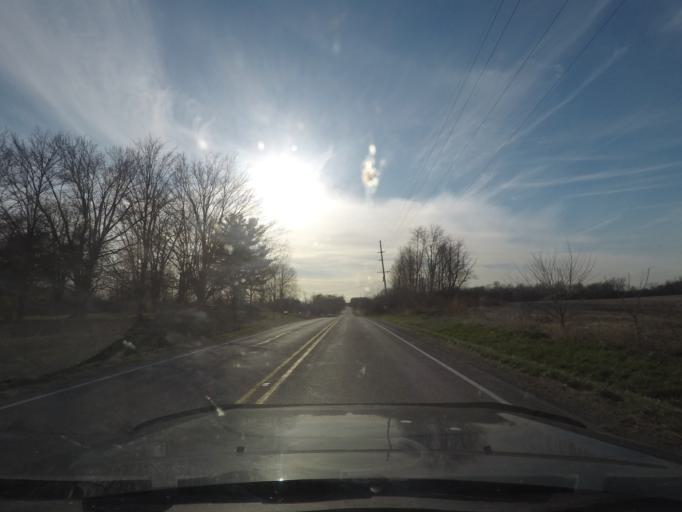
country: US
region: Indiana
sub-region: Saint Joseph County
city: Walkerton
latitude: 41.4481
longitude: -86.4083
